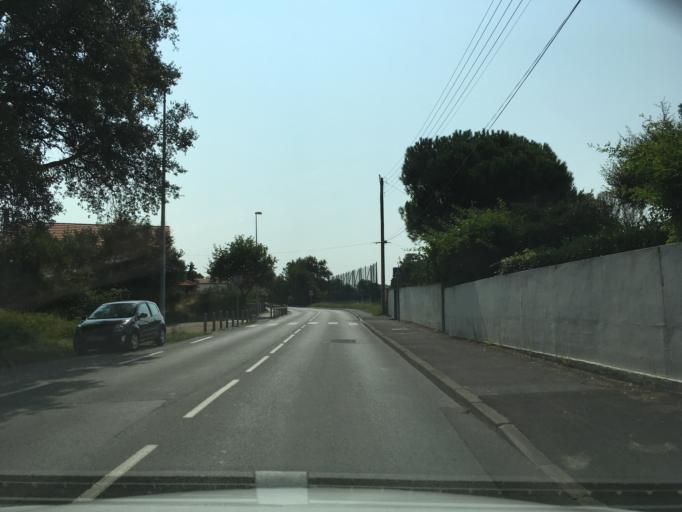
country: FR
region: Aquitaine
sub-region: Departement des Pyrenees-Atlantiques
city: Anglet
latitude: 43.5072
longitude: -1.5233
